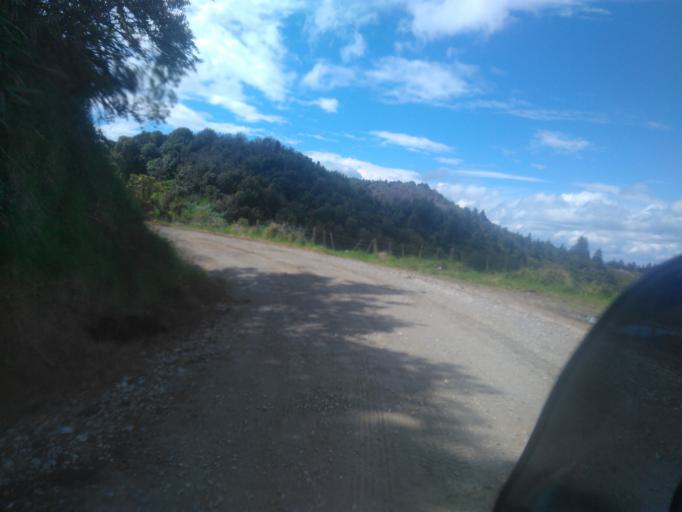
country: NZ
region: Hawke's Bay
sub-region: Wairoa District
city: Wairoa
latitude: -38.7788
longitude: 177.6224
